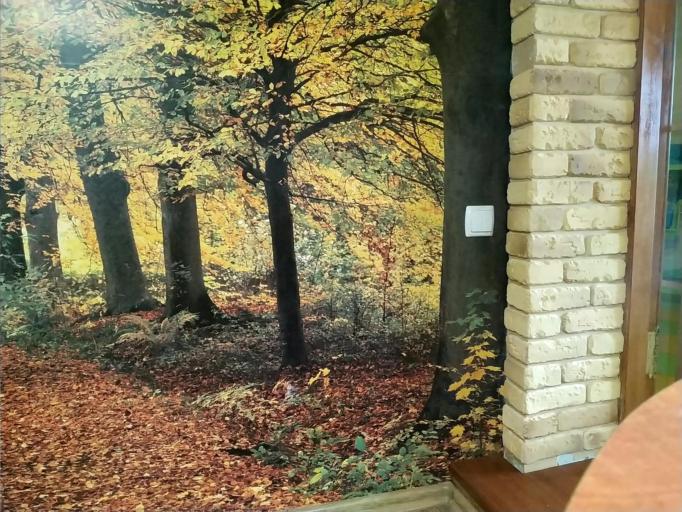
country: BY
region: Mogilev
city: Khotsimsk
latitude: 53.5489
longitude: 32.5140
